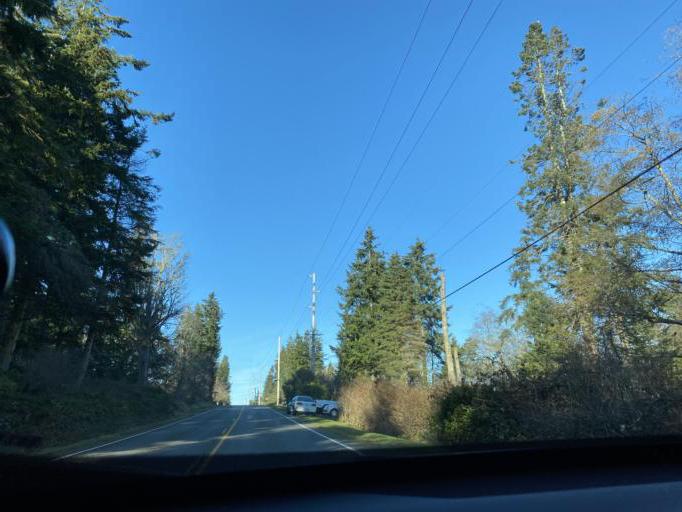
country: US
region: Washington
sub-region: Island County
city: Camano
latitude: 48.1222
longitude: -122.5628
